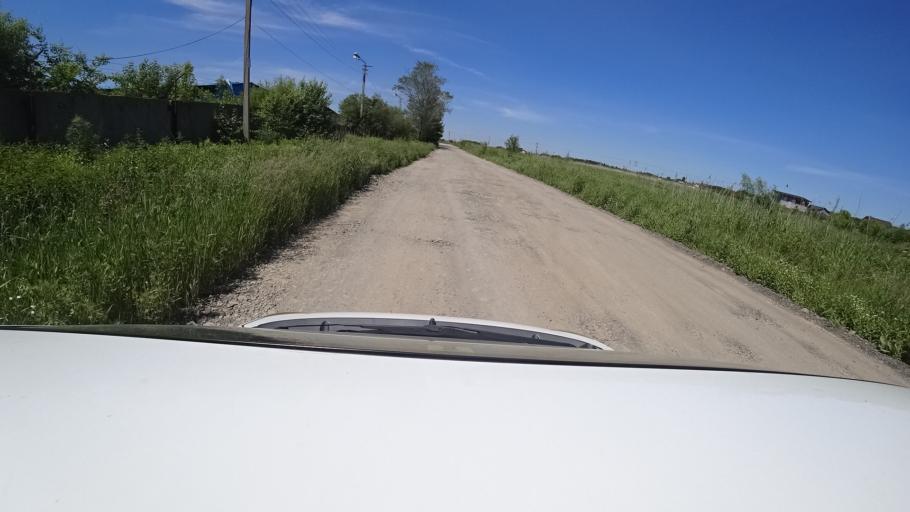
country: RU
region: Khabarovsk Krai
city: Topolevo
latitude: 48.5114
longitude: 135.1926
